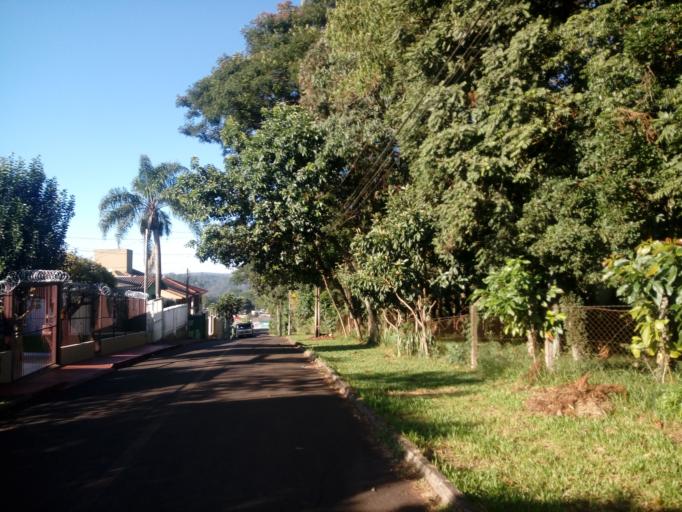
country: BR
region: Santa Catarina
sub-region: Chapeco
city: Chapeco
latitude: -27.0995
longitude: -52.6418
